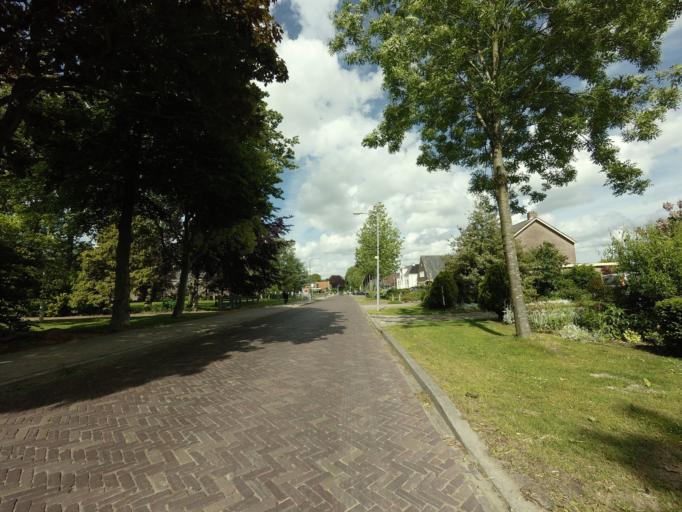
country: NL
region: North Holland
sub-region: Gemeente Hoorn
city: Hoorn
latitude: 52.6892
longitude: 5.0587
